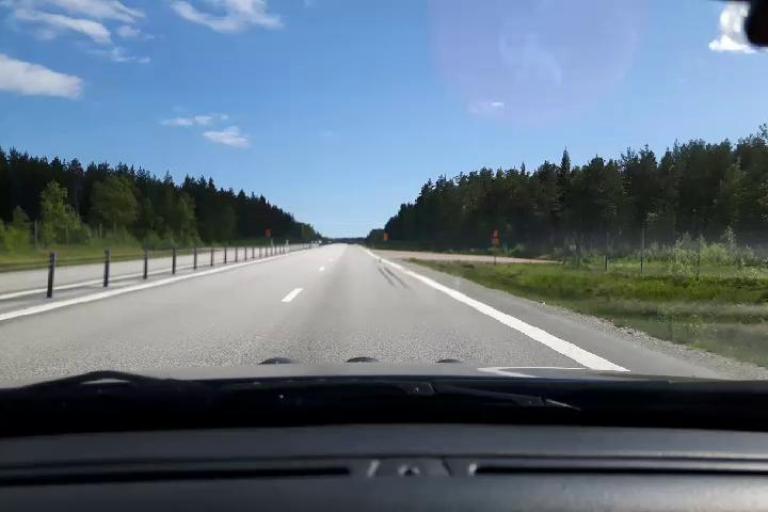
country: SE
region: Gaevleborg
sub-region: Hudiksvalls Kommun
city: Hudiksvall
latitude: 61.7077
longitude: 17.0499
